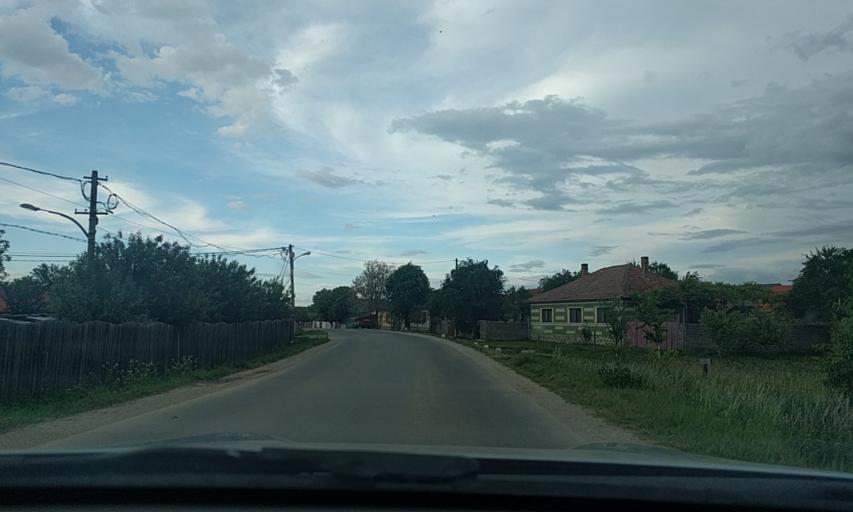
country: RO
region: Brasov
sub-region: Comuna Harman
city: Harman
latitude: 45.7559
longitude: 25.7167
